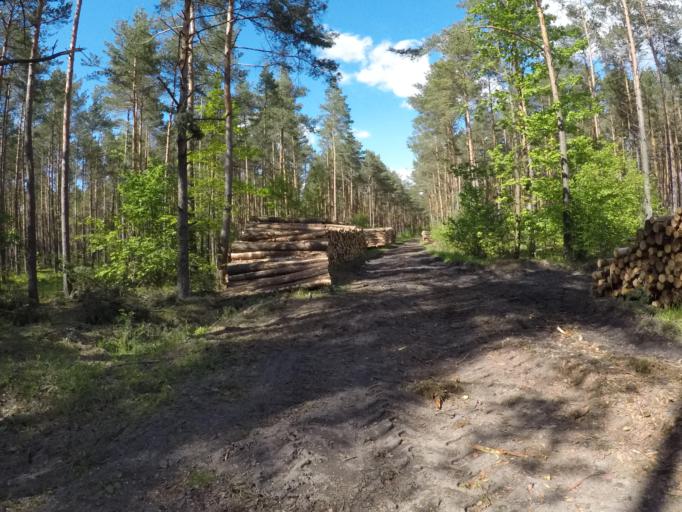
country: PL
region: Swietokrzyskie
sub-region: Powiat kielecki
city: Kostomloty Drugie
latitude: 50.8897
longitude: 20.5384
